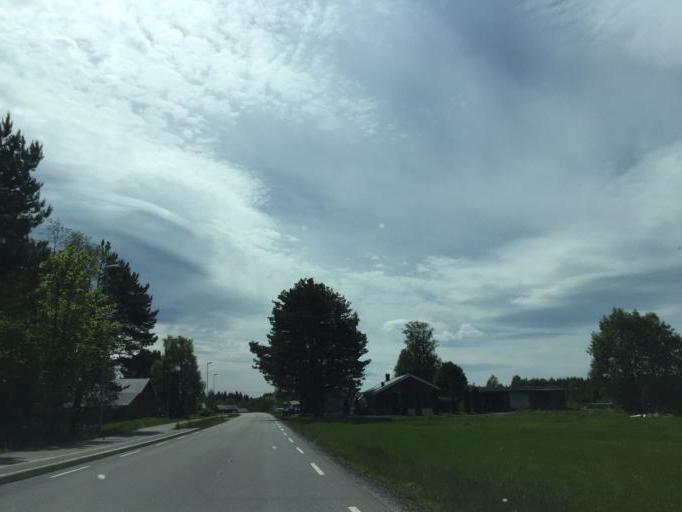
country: NO
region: Akershus
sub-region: Nes
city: Fjellfoten
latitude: 60.1057
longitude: 11.4792
